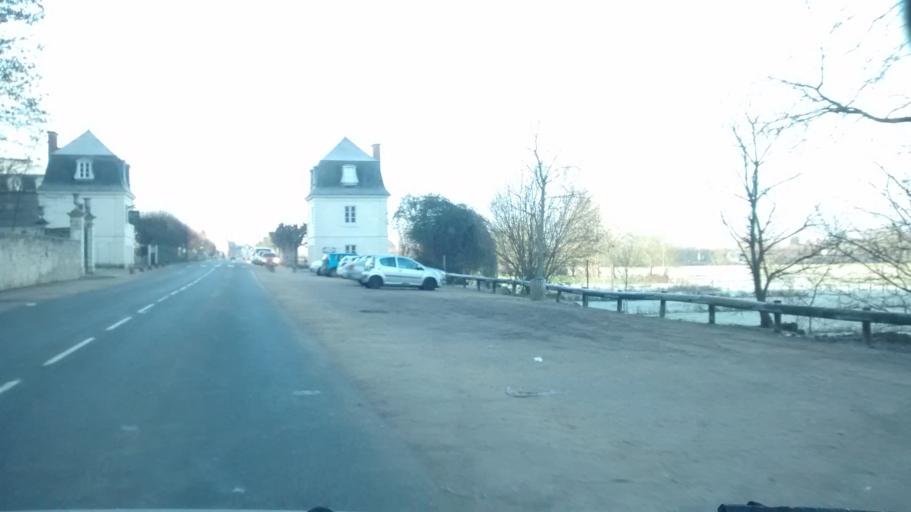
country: FR
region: Centre
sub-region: Departement d'Indre-et-Loire
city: Villandry
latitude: 47.3419
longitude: 0.5157
